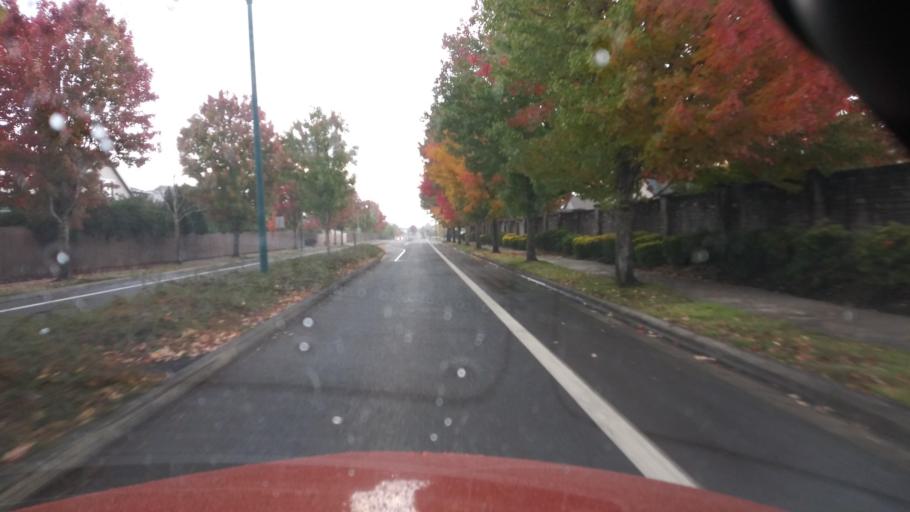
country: US
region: Oregon
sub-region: Washington County
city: Forest Grove
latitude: 45.5392
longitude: -123.1258
